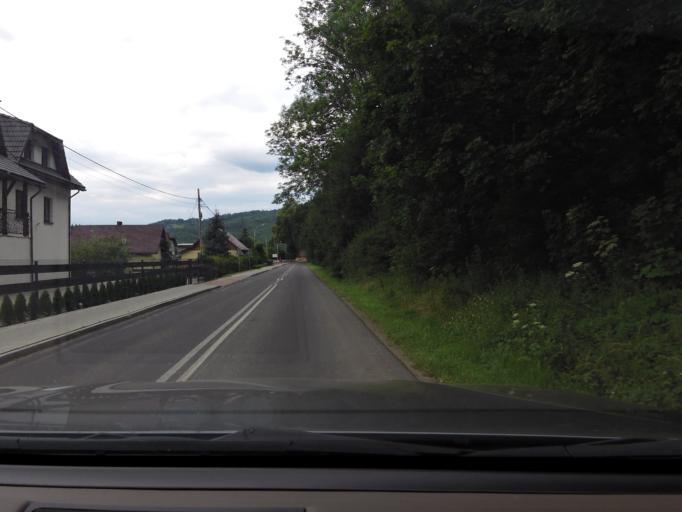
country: PL
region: Silesian Voivodeship
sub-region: Powiat zywiecki
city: Rajcza
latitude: 49.4956
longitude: 19.1044
